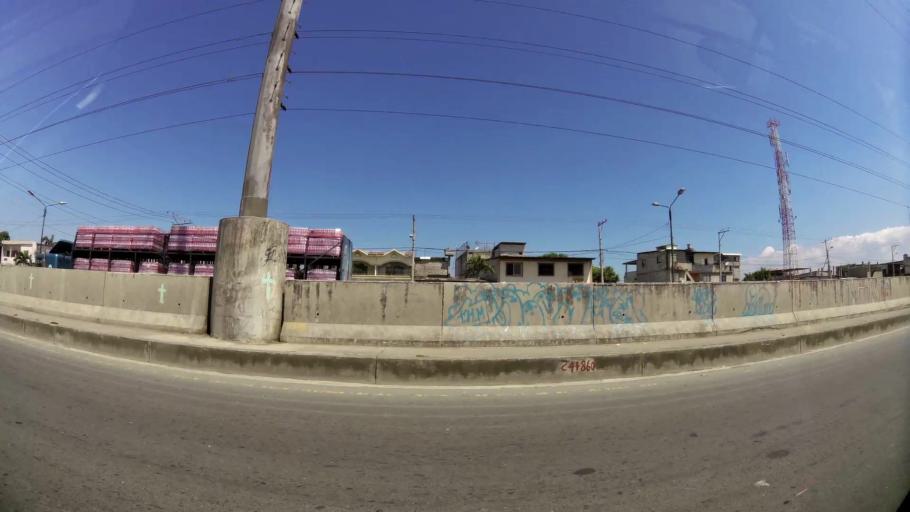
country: EC
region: Guayas
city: Guayaquil
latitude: -2.2384
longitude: -79.9256
